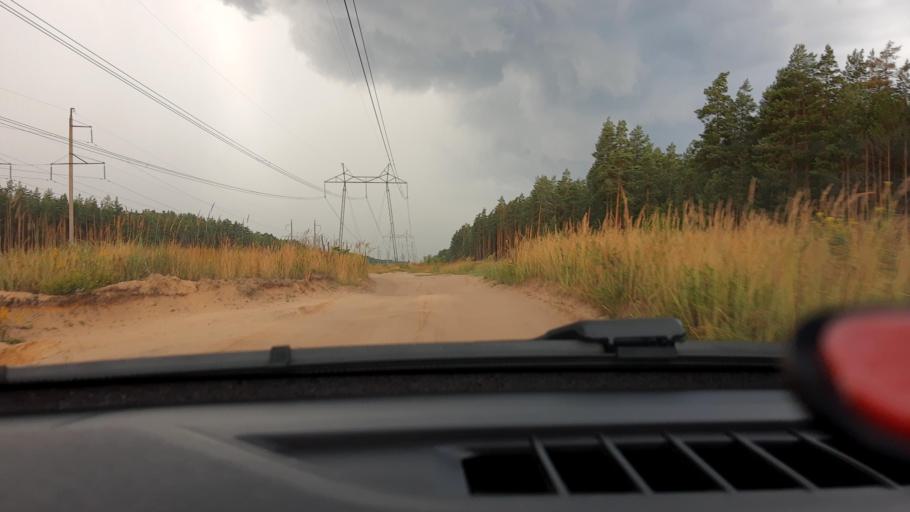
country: RU
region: Nizjnij Novgorod
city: Lukino
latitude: 56.3906
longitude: 43.6797
